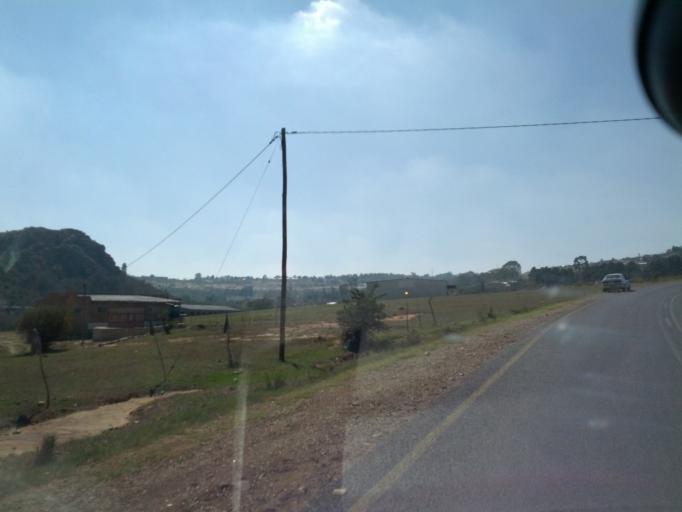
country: LS
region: Berea
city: Teyateyaneng
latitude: -29.1446
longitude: 27.7192
